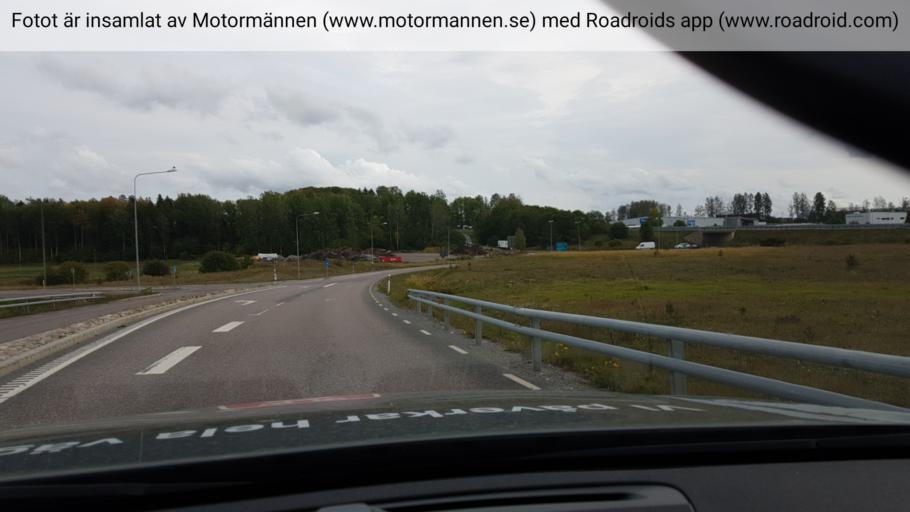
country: SE
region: Stockholm
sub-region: Norrtalje Kommun
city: Norrtalje
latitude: 59.7440
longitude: 18.6873
